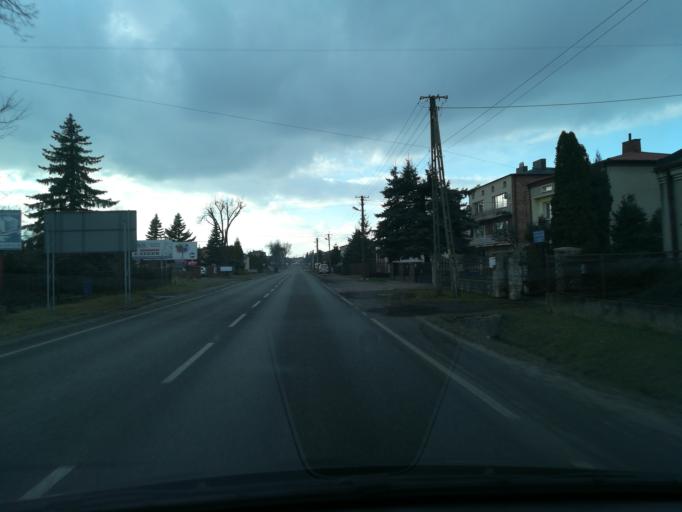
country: PL
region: Lodz Voivodeship
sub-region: Powiat radomszczanski
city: Radomsko
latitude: 51.0748
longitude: 19.4088
